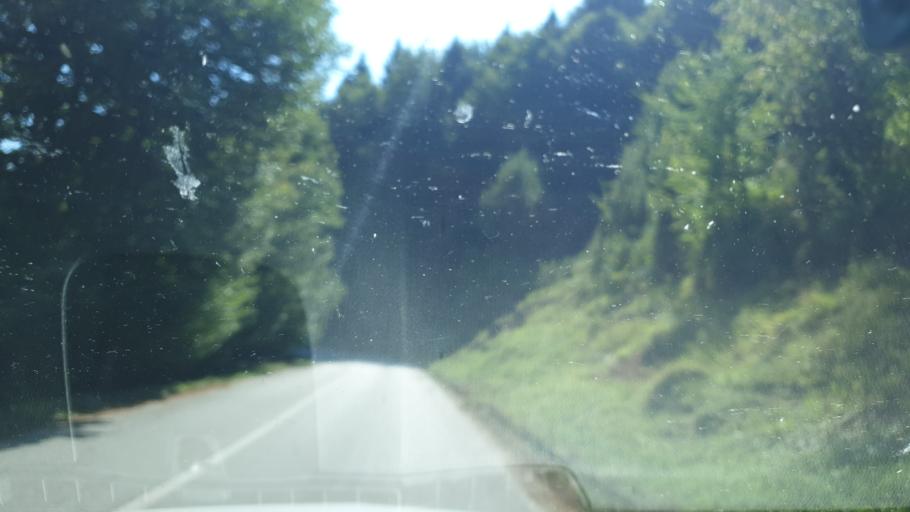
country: RS
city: Zlatibor
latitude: 43.6613
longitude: 19.8276
